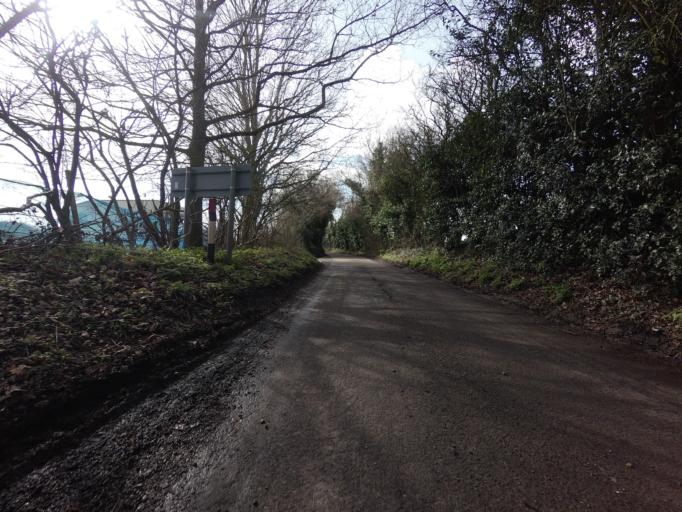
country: GB
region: England
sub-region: Kent
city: Swanley
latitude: 51.3742
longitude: 0.1581
